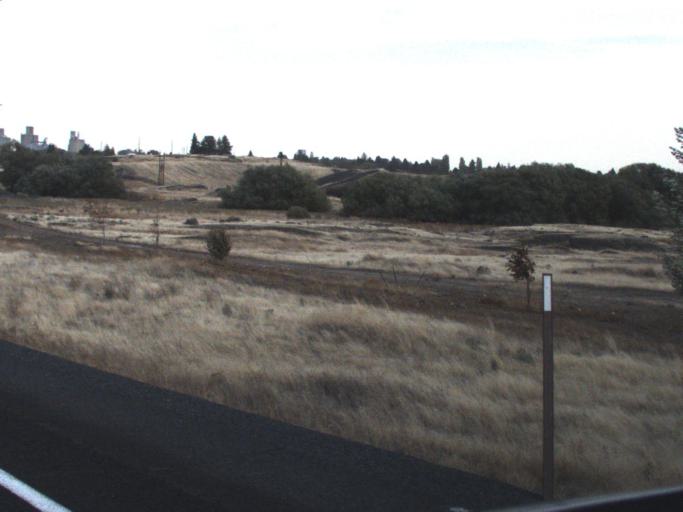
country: US
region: Washington
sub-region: Lincoln County
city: Davenport
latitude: 47.4771
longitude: -118.2705
